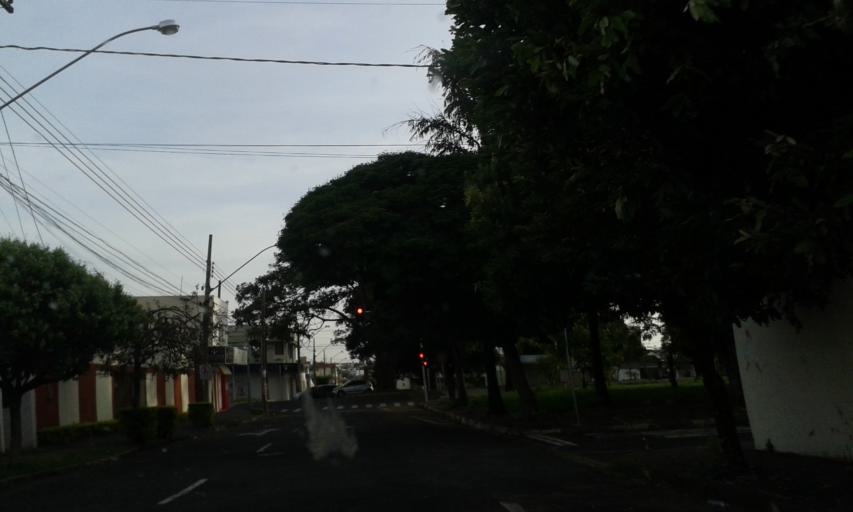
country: BR
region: Minas Gerais
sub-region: Uberlandia
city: Uberlandia
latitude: -18.9185
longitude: -48.2514
